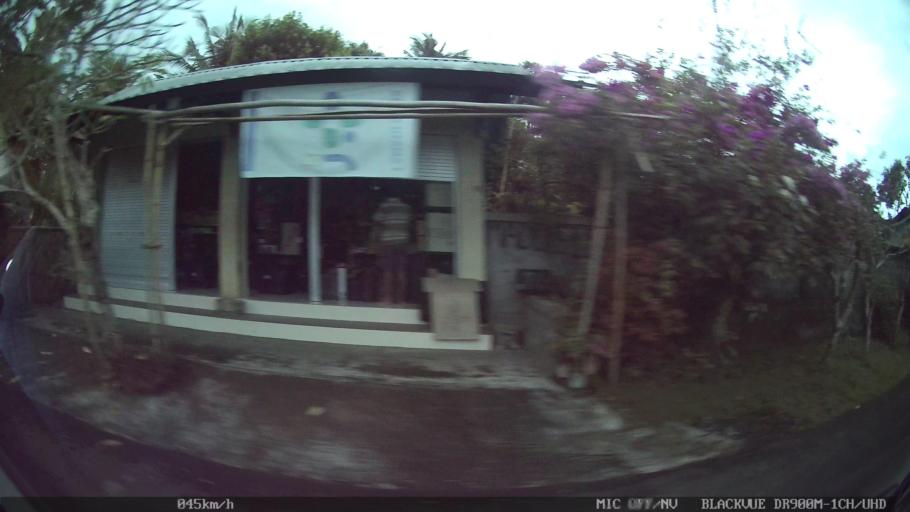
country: ID
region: Bali
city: Banjar Cemenggon
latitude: -8.5357
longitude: 115.1920
